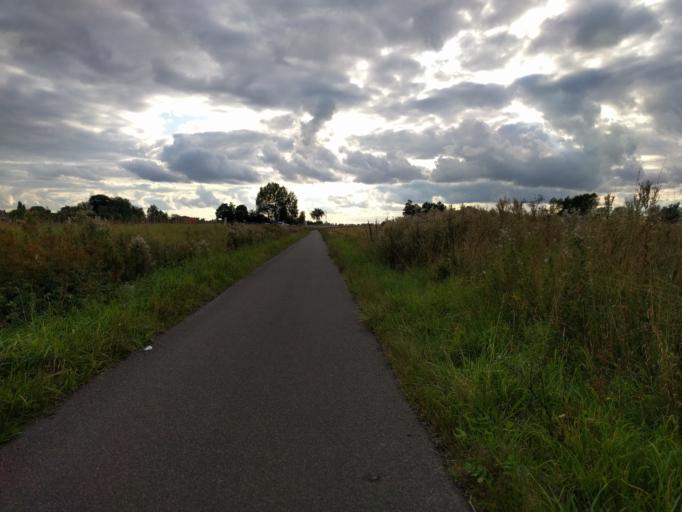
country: DK
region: South Denmark
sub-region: Odense Kommune
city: Bullerup
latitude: 55.4390
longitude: 10.5111
